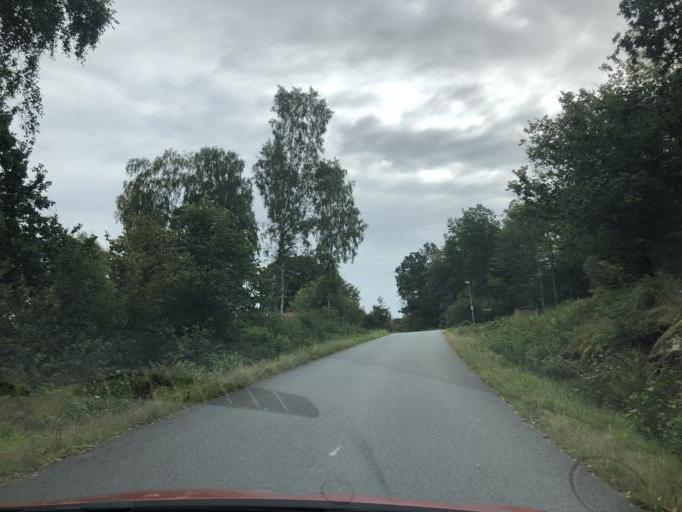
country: SE
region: Blekinge
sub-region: Solvesborgs Kommun
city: Soelvesborg
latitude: 56.1413
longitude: 14.5871
